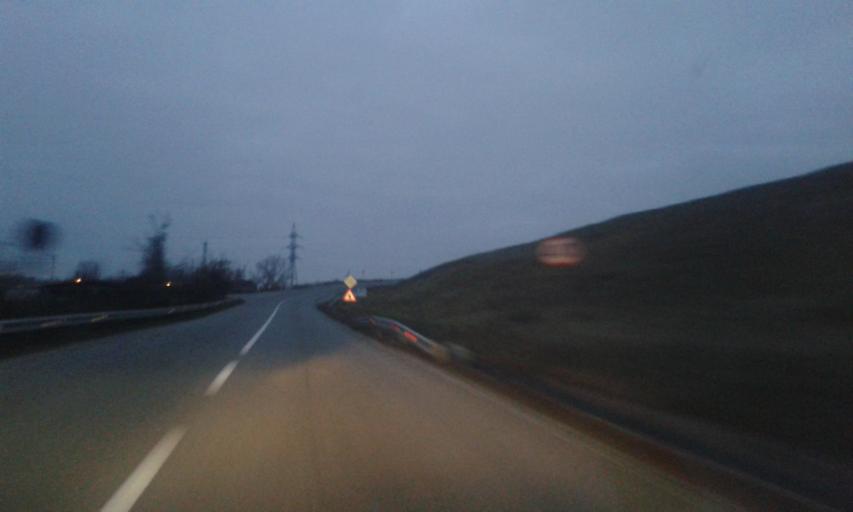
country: RO
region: Gorj
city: Targu Jiu
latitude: 45.0595
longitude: 23.2730
